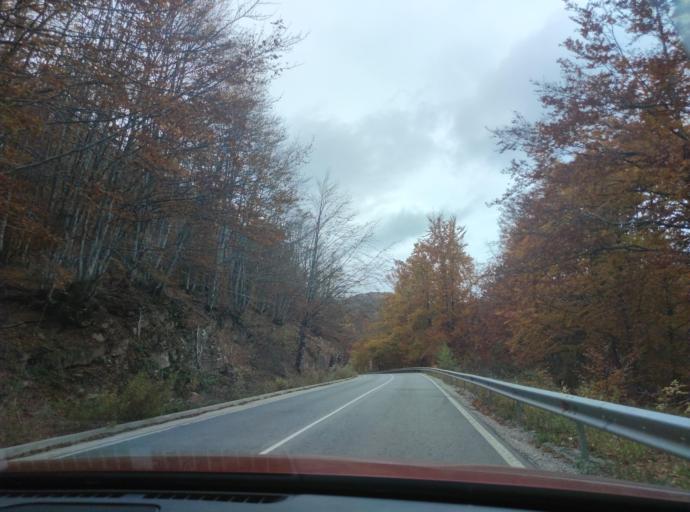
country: BG
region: Sofiya
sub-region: Obshtina Godech
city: Godech
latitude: 43.1076
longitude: 23.1046
